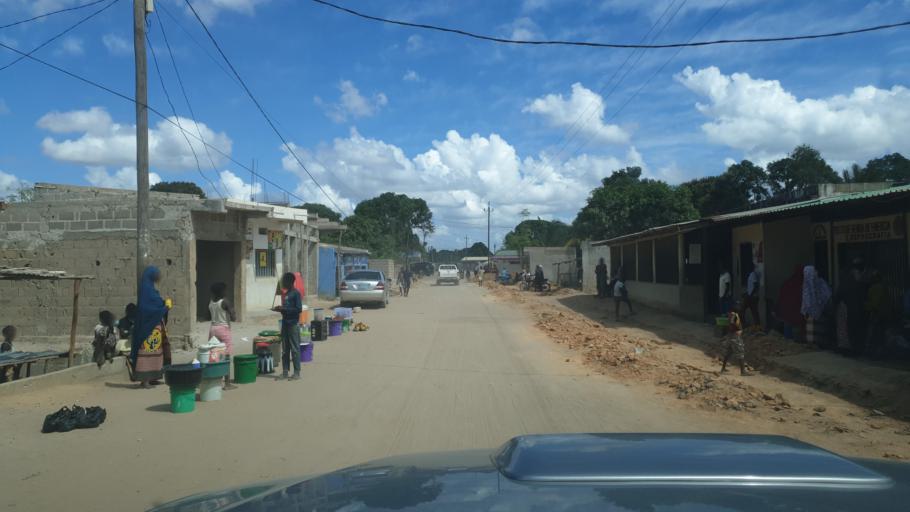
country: MZ
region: Nampula
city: Nacala
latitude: -14.5655
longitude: 40.7012
